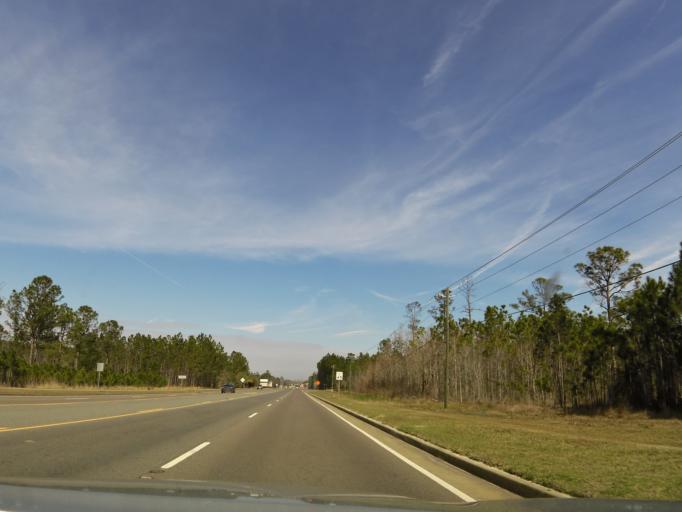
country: US
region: Georgia
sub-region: Ware County
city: Deenwood
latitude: 31.2014
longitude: -82.3838
